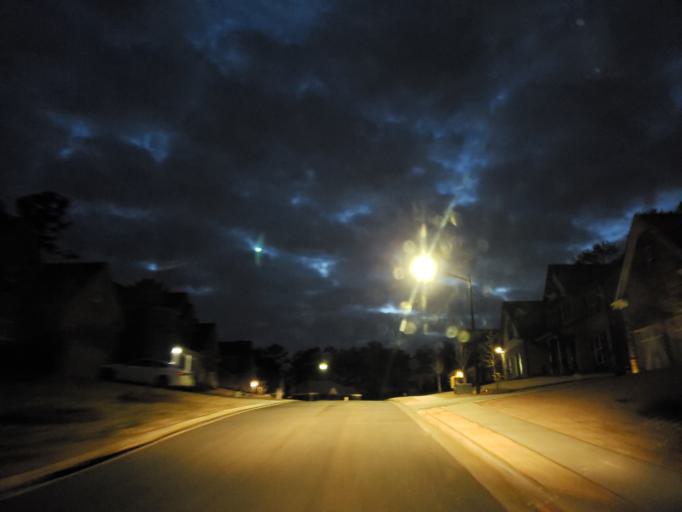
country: US
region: Georgia
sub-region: Cobb County
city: Kennesaw
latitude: 33.9838
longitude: -84.6268
